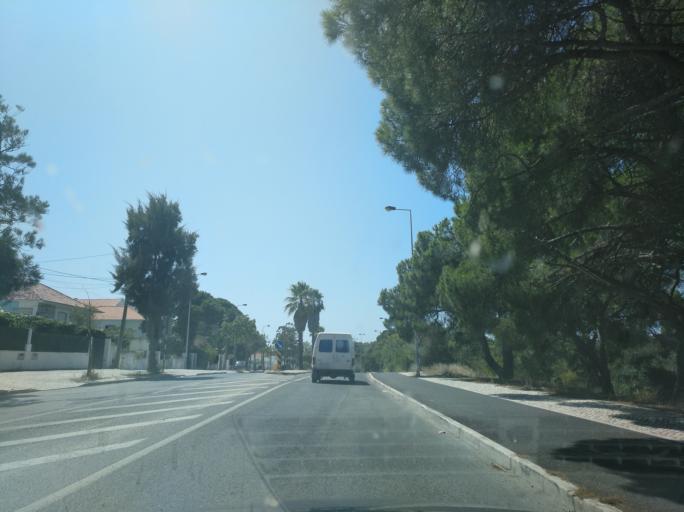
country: PT
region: Setubal
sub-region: Almada
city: Trafaria
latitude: 38.6670
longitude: -9.2409
